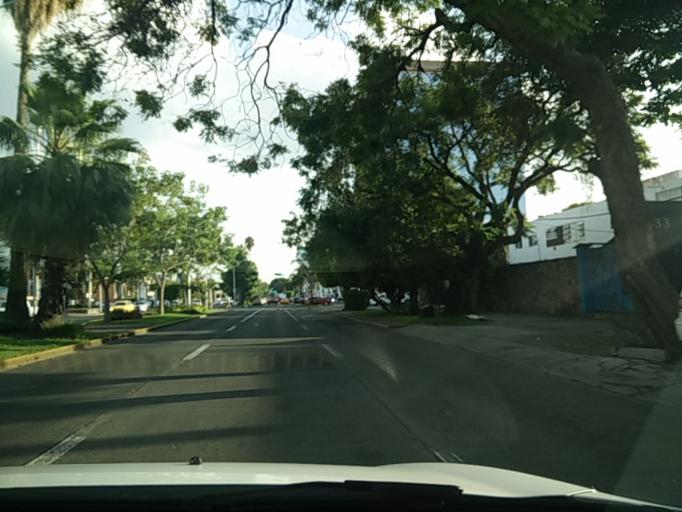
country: MX
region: Jalisco
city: Guadalajara
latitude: 20.6881
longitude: -103.3735
